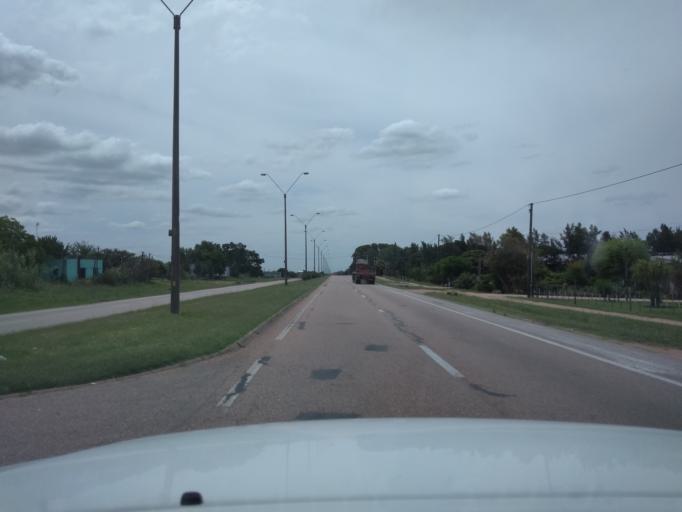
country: UY
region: Canelones
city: Joanico
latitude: -34.5891
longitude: -56.2630
